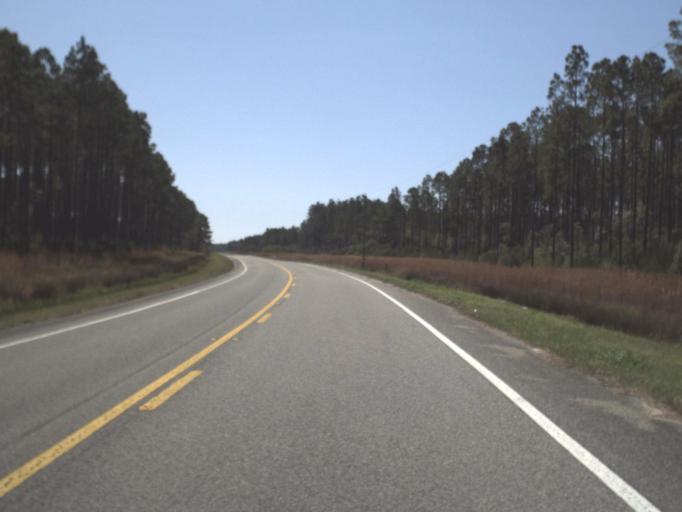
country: US
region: Florida
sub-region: Leon County
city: Woodville
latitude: 30.2187
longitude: -84.0494
